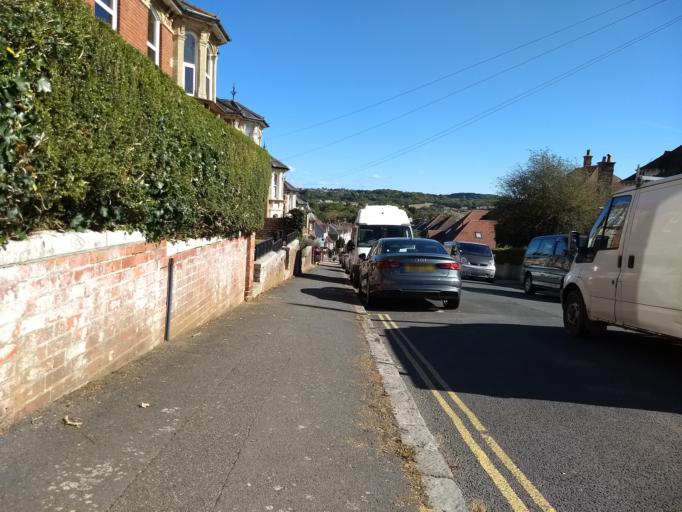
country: GB
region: England
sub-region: Isle of Wight
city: Newport
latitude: 50.6938
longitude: -1.2939
